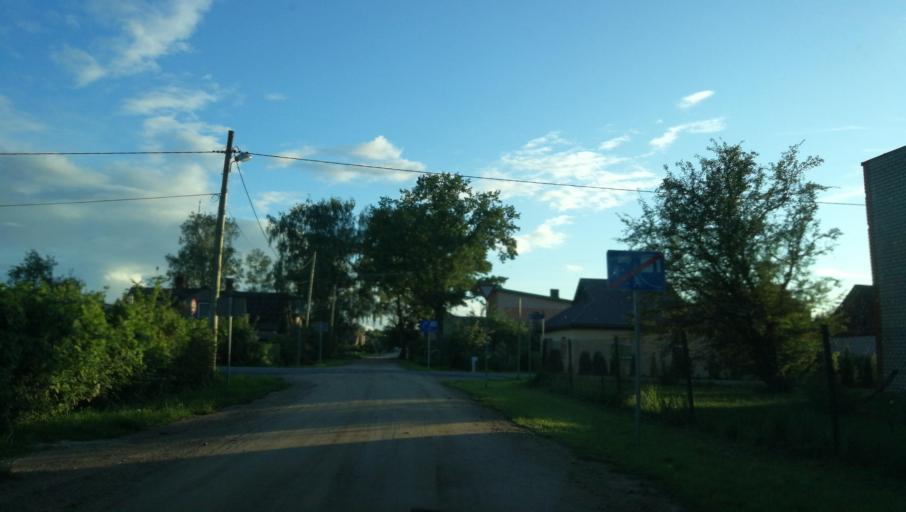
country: LV
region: Valmieras Rajons
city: Valmiera
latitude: 57.5349
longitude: 25.3955
